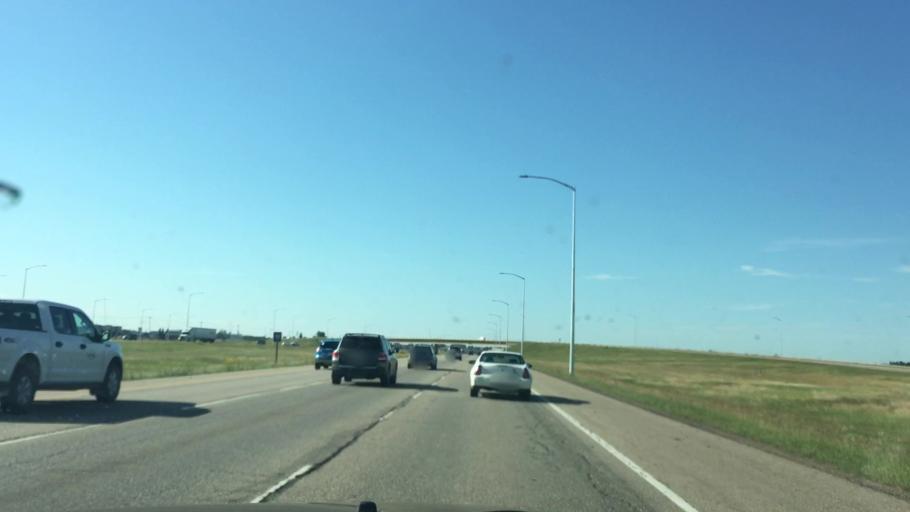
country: CA
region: Alberta
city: Leduc
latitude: 53.2890
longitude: -113.5499
